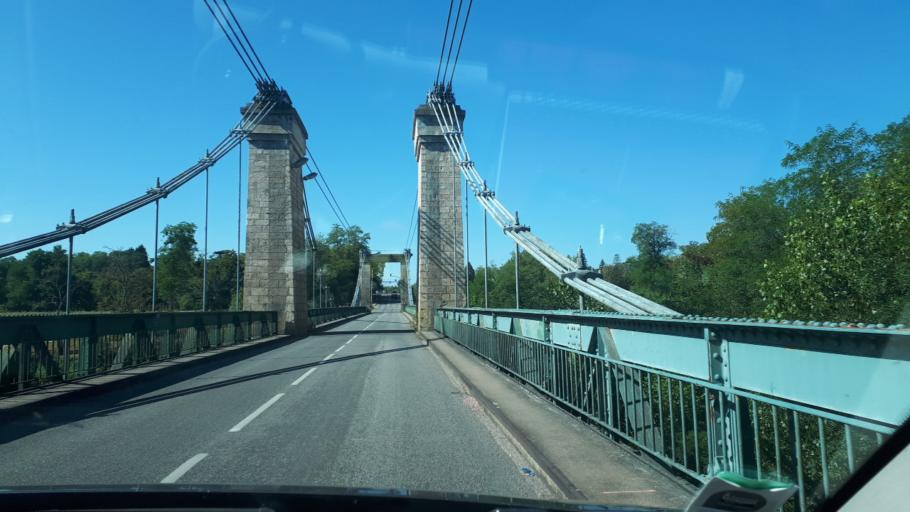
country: FR
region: Centre
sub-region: Departement du Loiret
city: Briare
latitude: 47.5976
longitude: 2.7604
